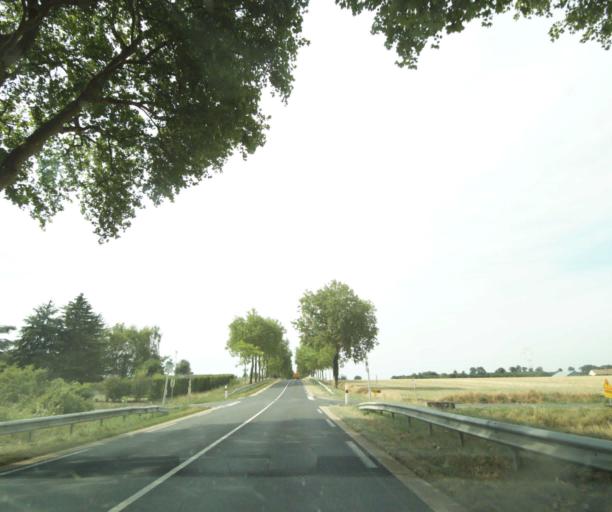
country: FR
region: Centre
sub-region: Departement d'Indre-et-Loire
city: Saint-Antoine-du-Rocher
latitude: 47.5082
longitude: 0.5947
